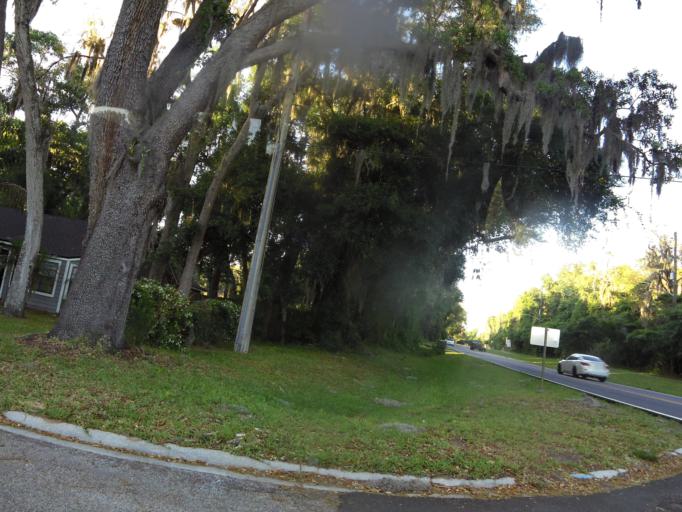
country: US
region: Florida
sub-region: Duval County
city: Atlantic Beach
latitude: 30.3685
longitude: -81.5155
